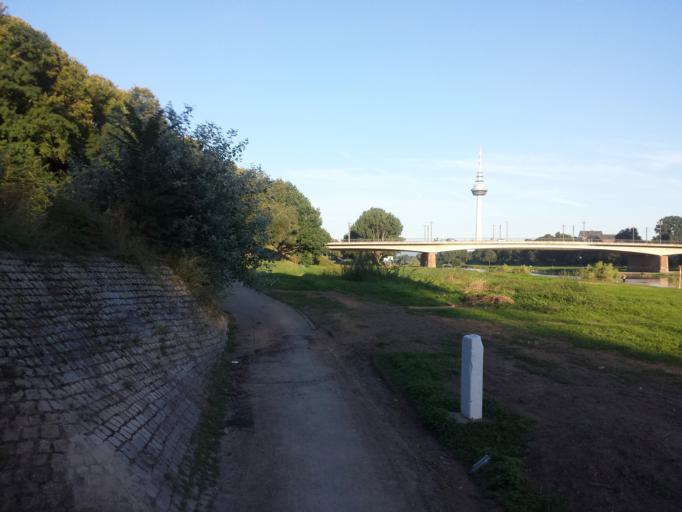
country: DE
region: Baden-Wuerttemberg
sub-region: Karlsruhe Region
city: Mannheim
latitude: 49.4929
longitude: 8.4790
